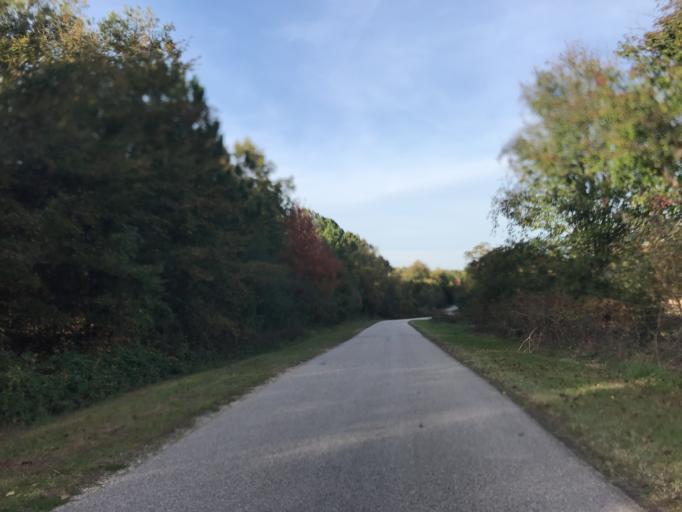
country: US
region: North Carolina
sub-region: Wake County
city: West Raleigh
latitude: 35.8000
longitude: -78.6931
